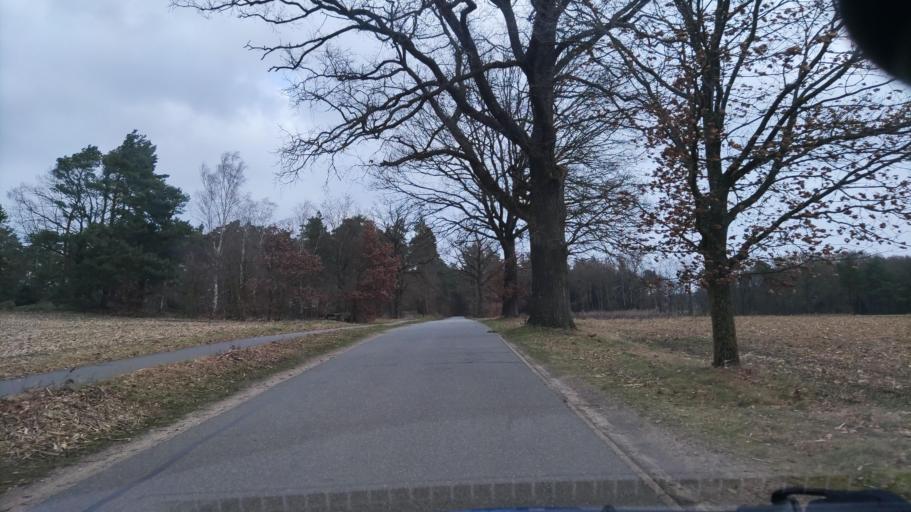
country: DE
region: Lower Saxony
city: Sudergellersen
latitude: 53.2079
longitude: 10.3204
